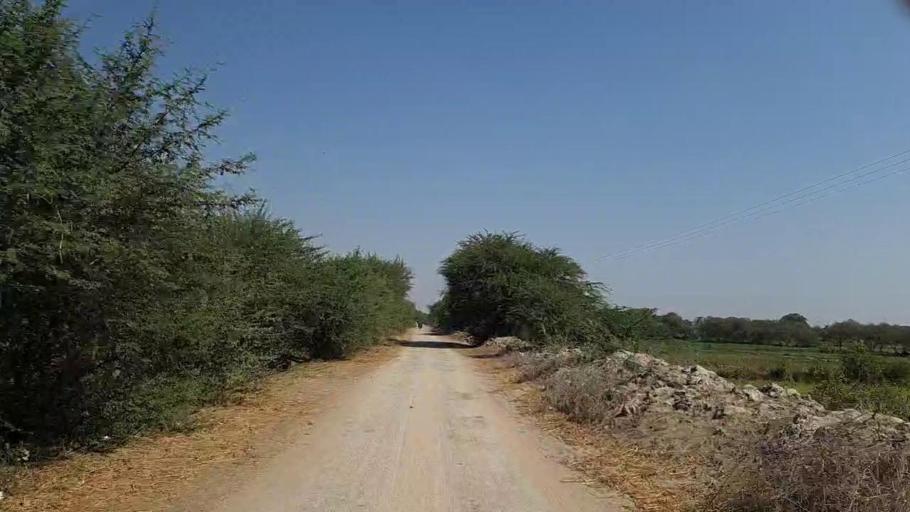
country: PK
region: Sindh
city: Mirpur Batoro
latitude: 24.6892
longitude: 68.2577
